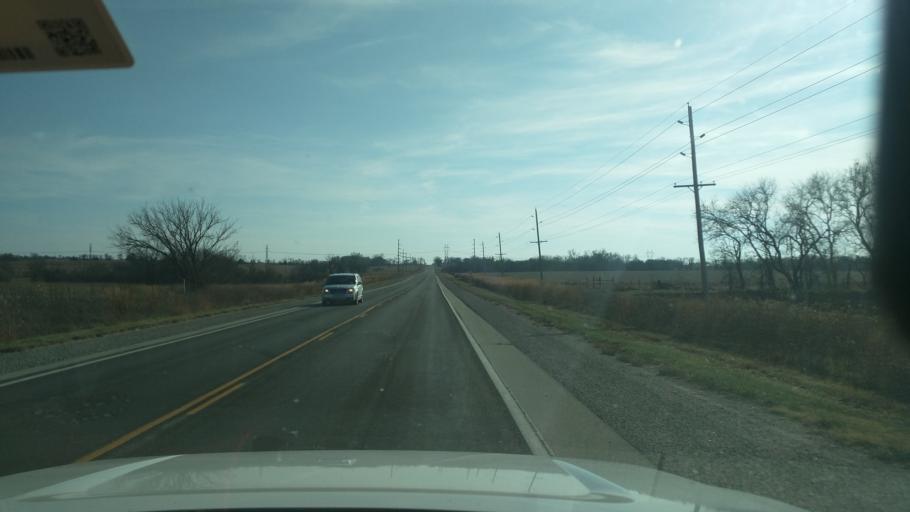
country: US
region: Kansas
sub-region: Lyon County
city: Emporia
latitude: 38.2970
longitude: -96.1805
